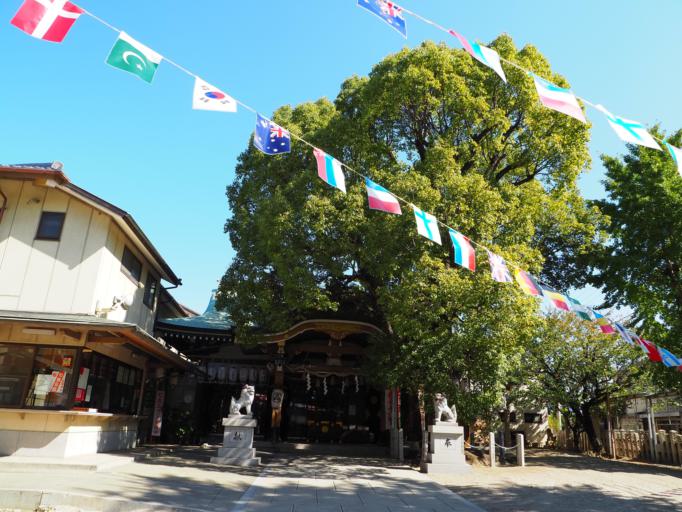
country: JP
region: Osaka
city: Sakai
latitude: 34.5544
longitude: 135.4619
